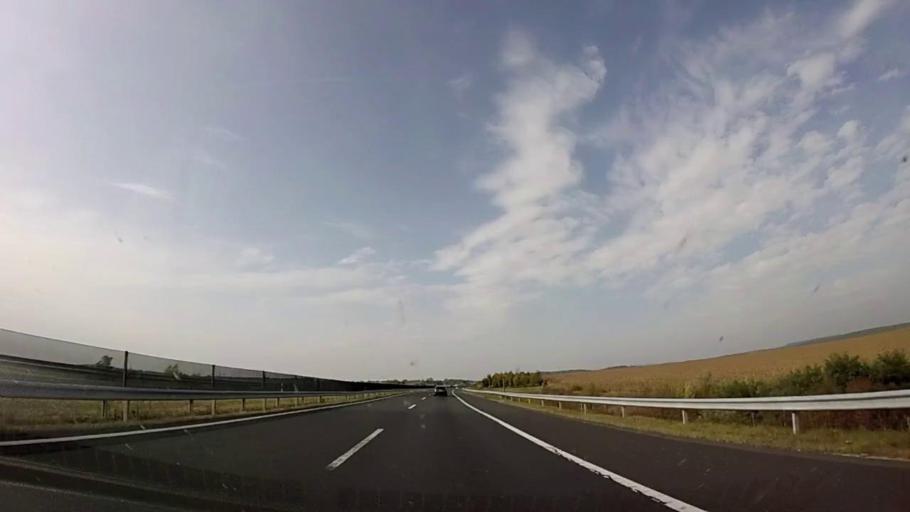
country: HU
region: Zala
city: Murakeresztur
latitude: 46.4497
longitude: 16.8682
